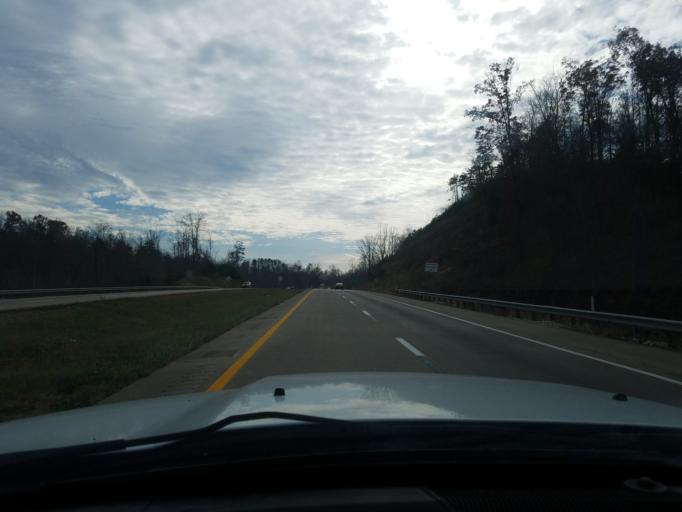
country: US
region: West Virginia
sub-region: Putnam County
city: Eleanor
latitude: 38.5057
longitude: -81.9316
